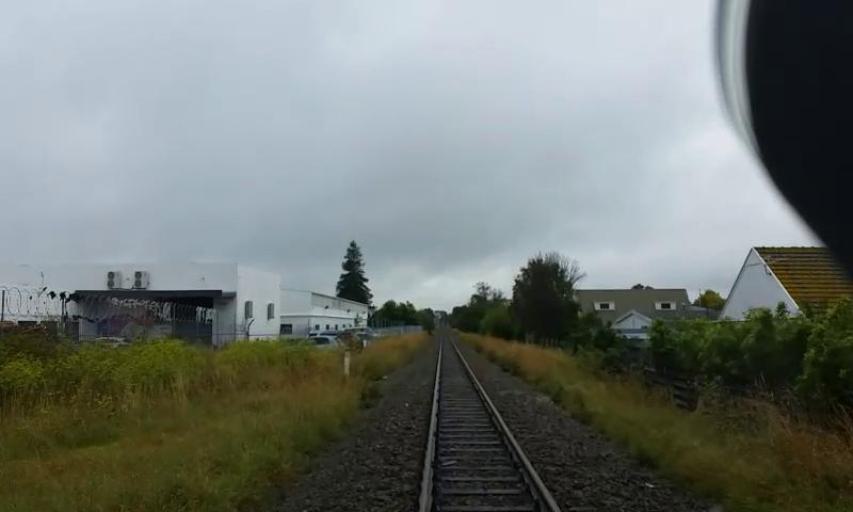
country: NZ
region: Canterbury
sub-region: Christchurch City
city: Christchurch
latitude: -43.5327
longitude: 172.6092
